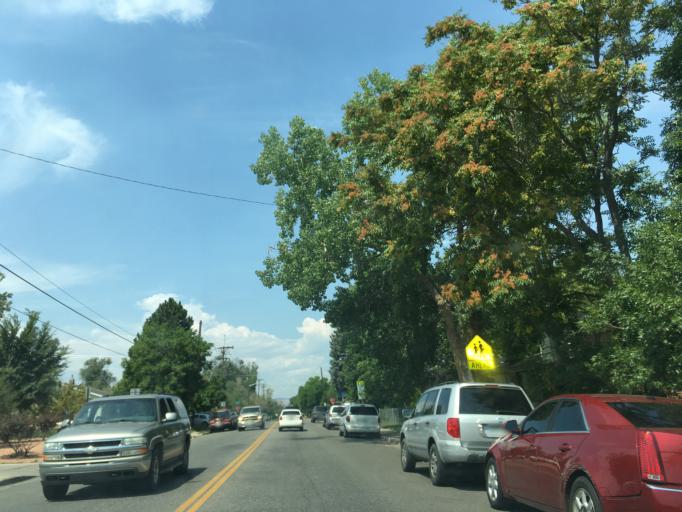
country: US
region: Colorado
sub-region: Jefferson County
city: Lakewood
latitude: 39.7004
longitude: -105.0332
